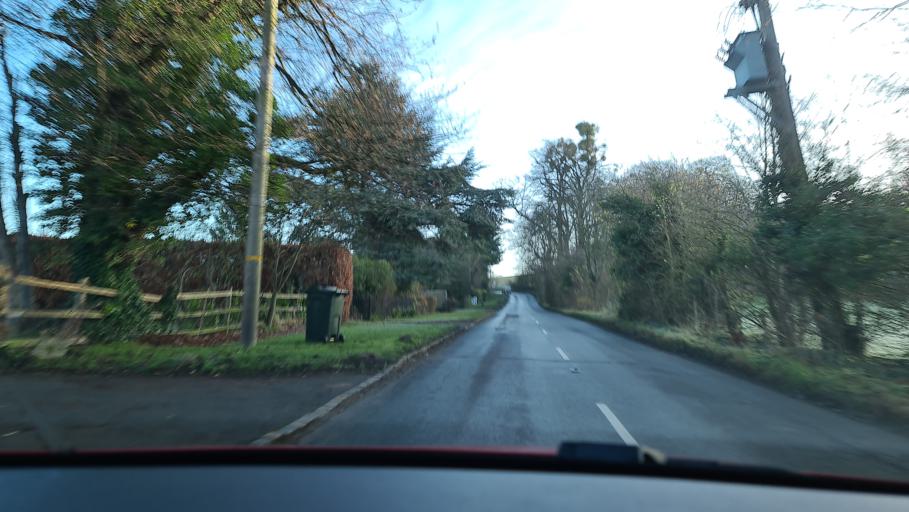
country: GB
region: England
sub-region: Buckinghamshire
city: Princes Risborough
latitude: 51.7514
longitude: -0.7987
